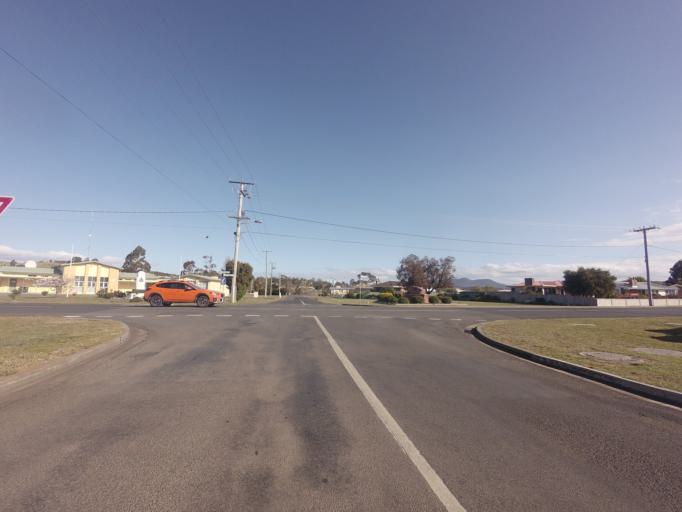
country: AU
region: Tasmania
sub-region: Sorell
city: Sorell
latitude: -42.5074
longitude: 147.9165
